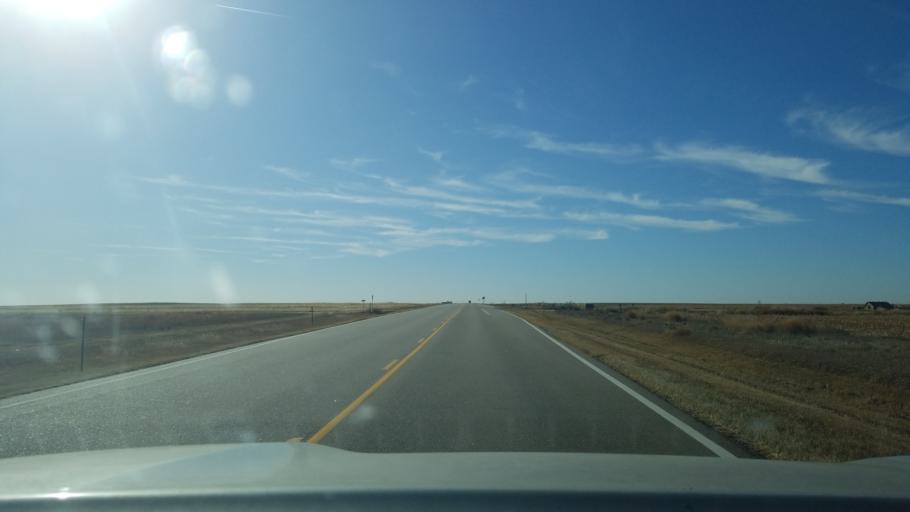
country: US
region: Kansas
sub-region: Ness County
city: Ness City
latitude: 38.3502
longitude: -99.8978
